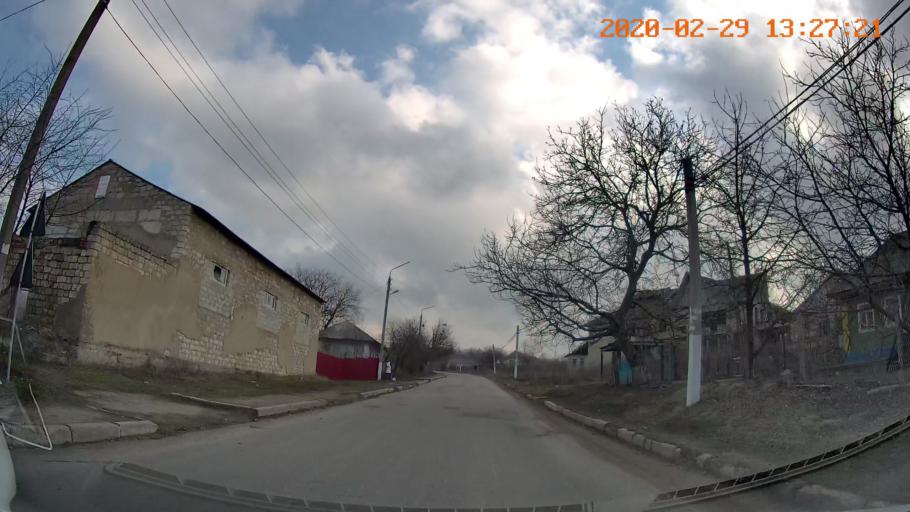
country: MD
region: Telenesti
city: Camenca
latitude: 47.9124
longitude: 28.6405
